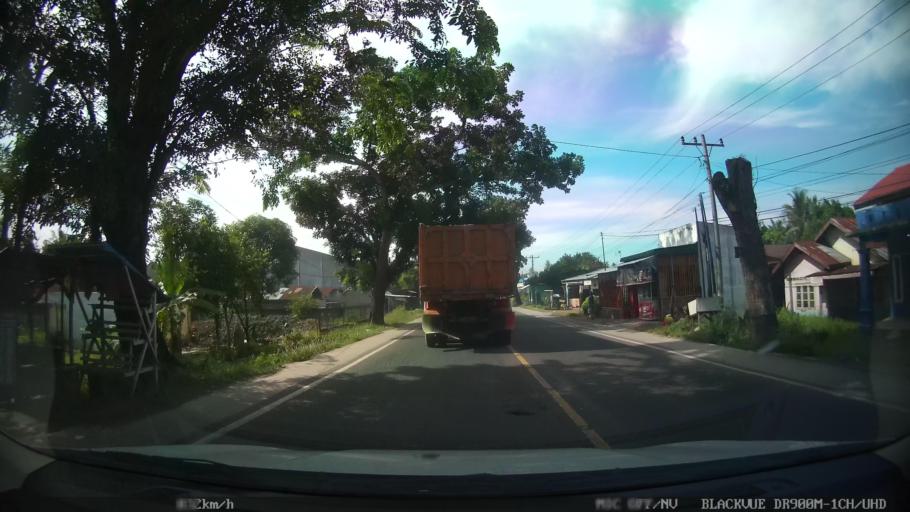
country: ID
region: North Sumatra
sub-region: Kabupaten Langkat
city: Stabat
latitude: 3.7105
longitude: 98.5057
